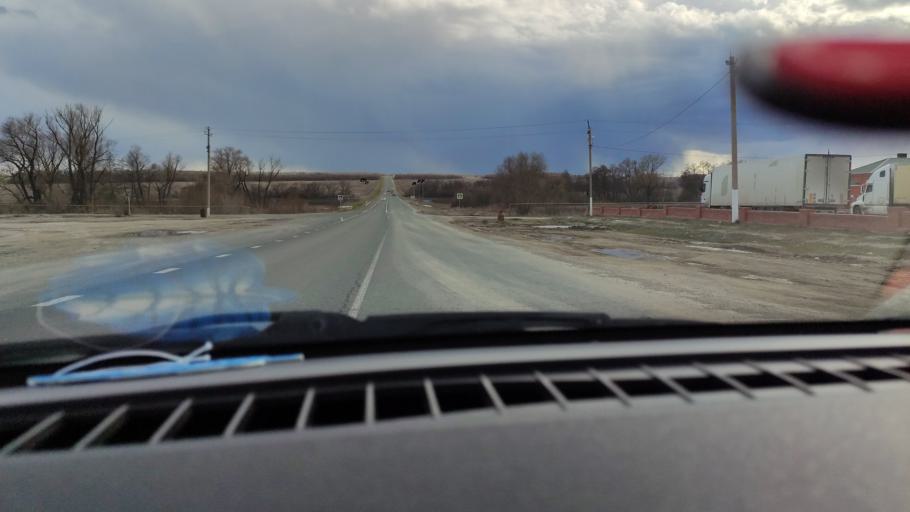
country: RU
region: Saratov
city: Sinodskoye
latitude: 51.9188
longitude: 46.5608
